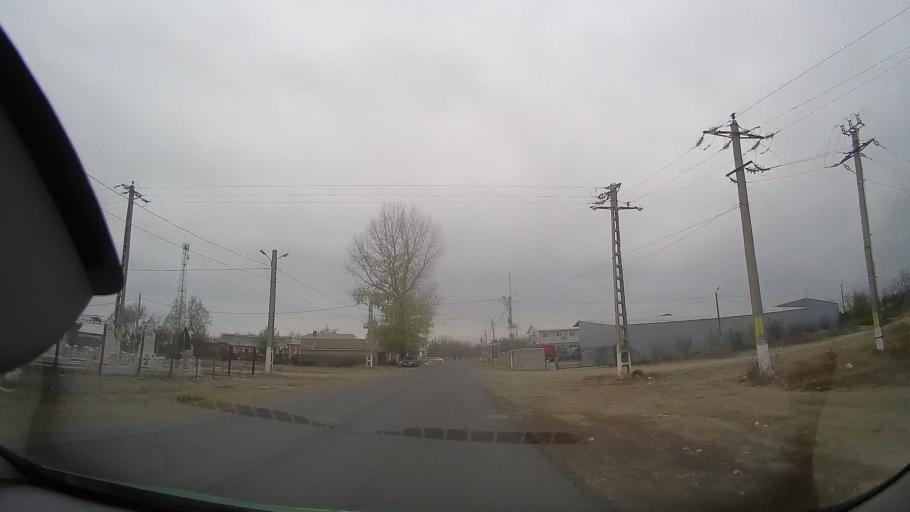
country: RO
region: Braila
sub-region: Comuna Ulmu
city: Ulmu
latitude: 44.9442
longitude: 27.3333
